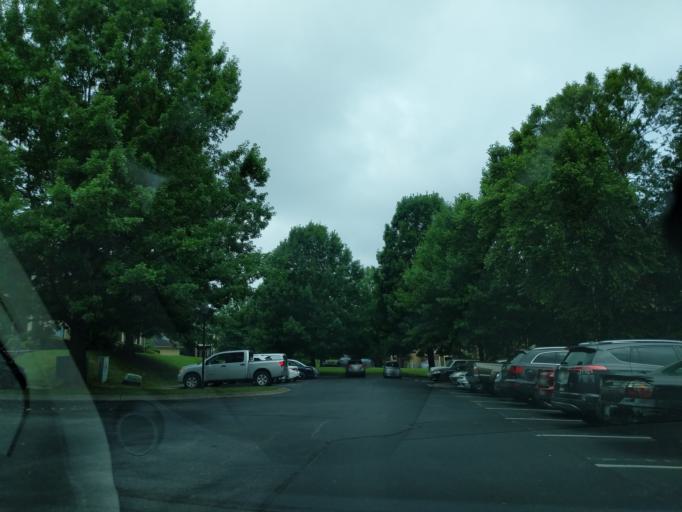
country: US
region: Tennessee
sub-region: Davidson County
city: Lakewood
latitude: 36.1720
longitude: -86.6107
